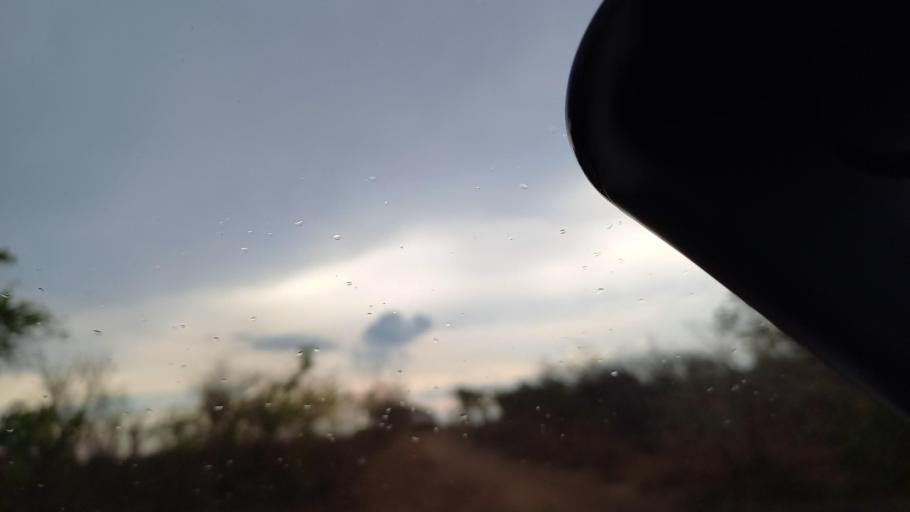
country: ZM
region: Lusaka
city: Kafue
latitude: -15.9922
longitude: 28.2725
